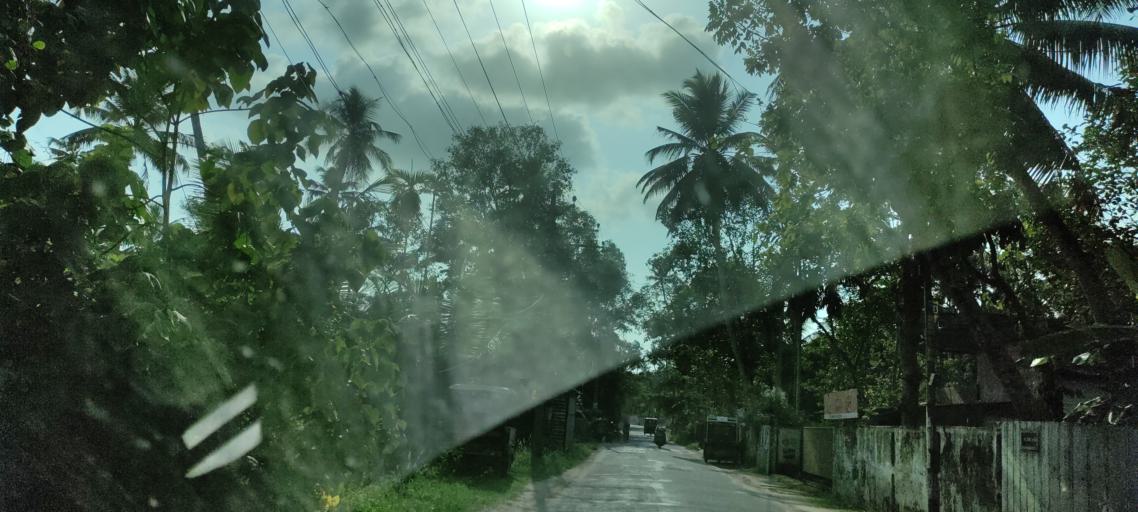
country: IN
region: Kerala
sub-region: Alappuzha
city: Vayalar
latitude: 9.6877
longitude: 76.3238
